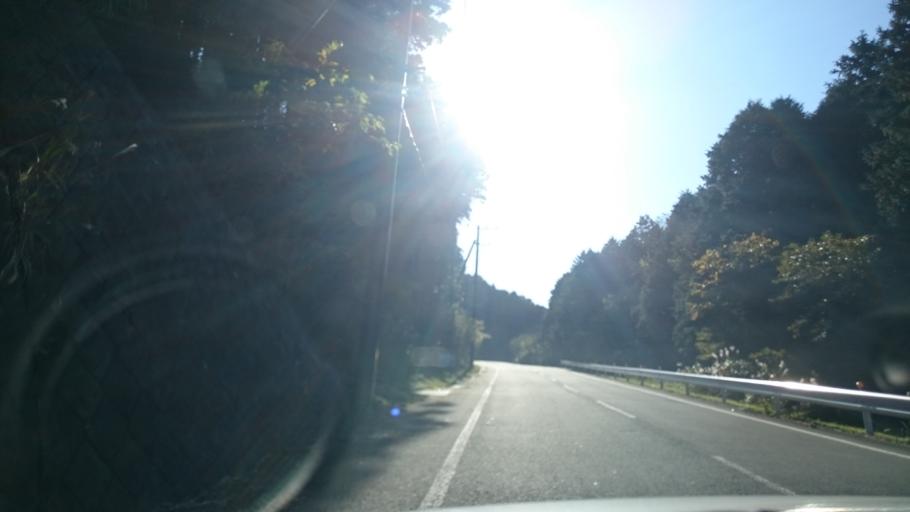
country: JP
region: Shizuoka
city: Heda
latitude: 34.9866
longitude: 138.8100
